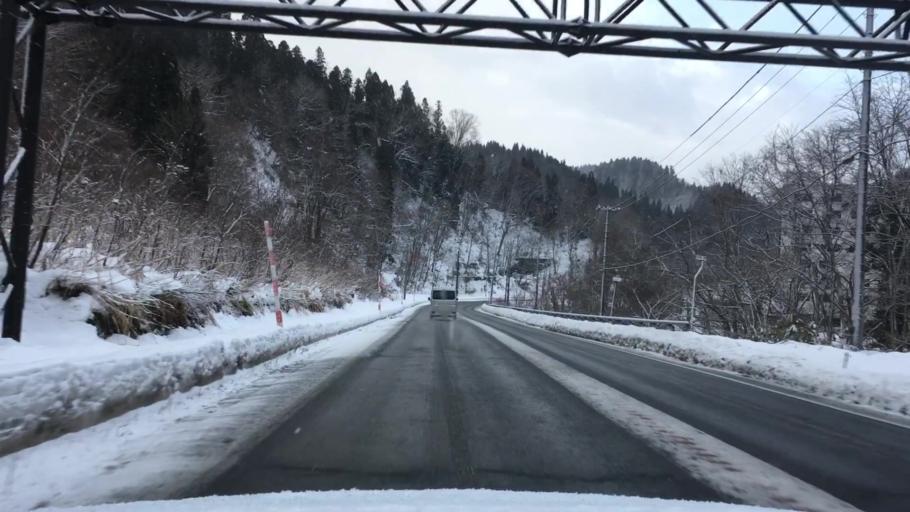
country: JP
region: Akita
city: Odate
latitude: 40.4284
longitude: 140.6369
